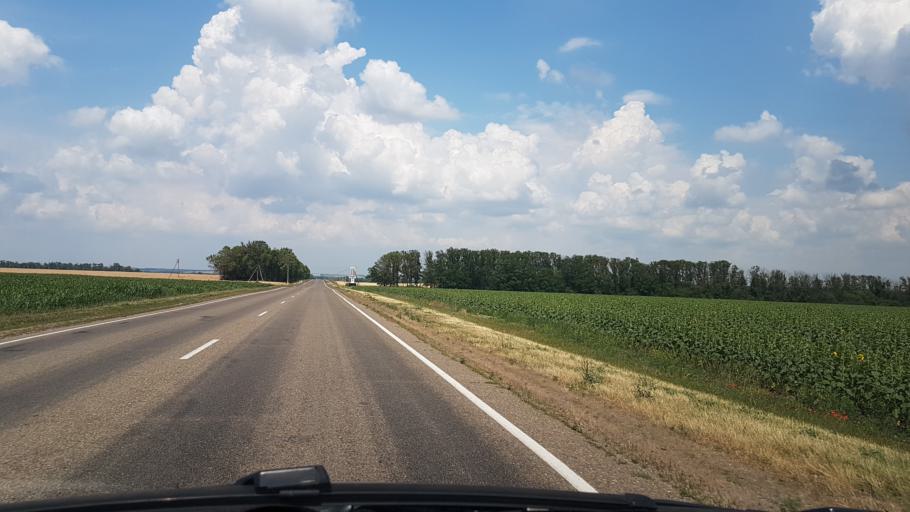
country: RU
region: Krasnodarskiy
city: Dmitriyevskaya
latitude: 45.6882
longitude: 40.7441
